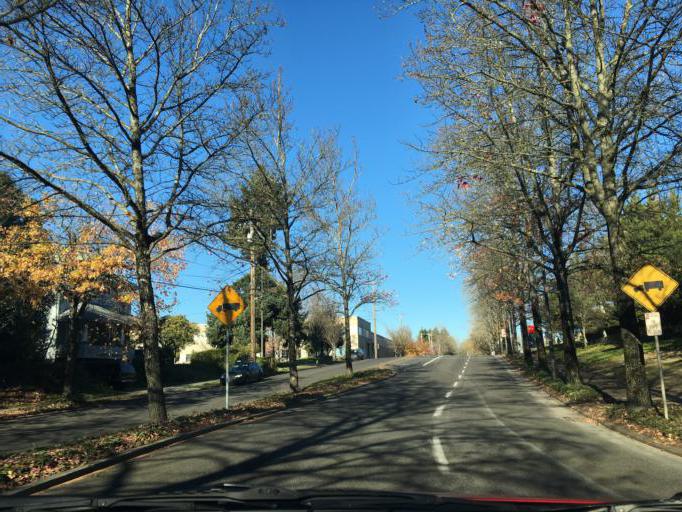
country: US
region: Oregon
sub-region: Multnomah County
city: Portland
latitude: 45.5418
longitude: -122.6718
